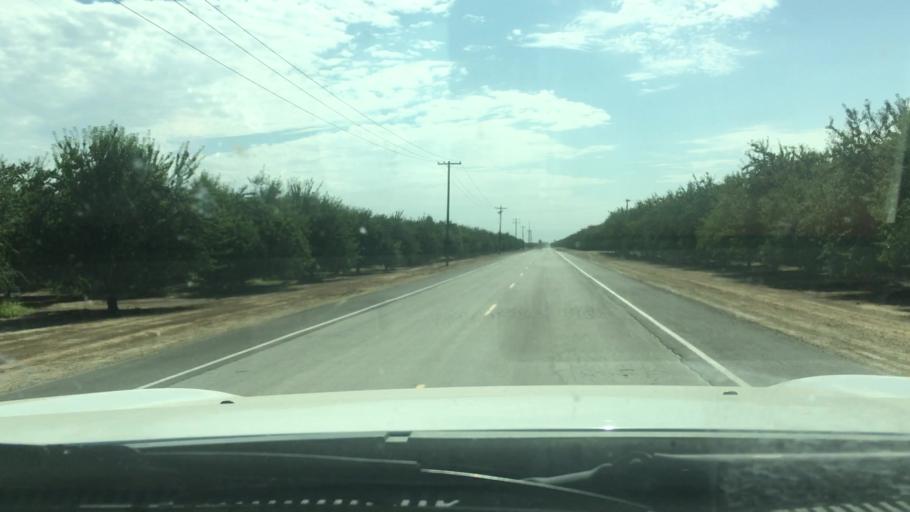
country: US
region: California
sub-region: Kern County
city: Wasco
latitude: 35.5578
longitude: -119.4452
